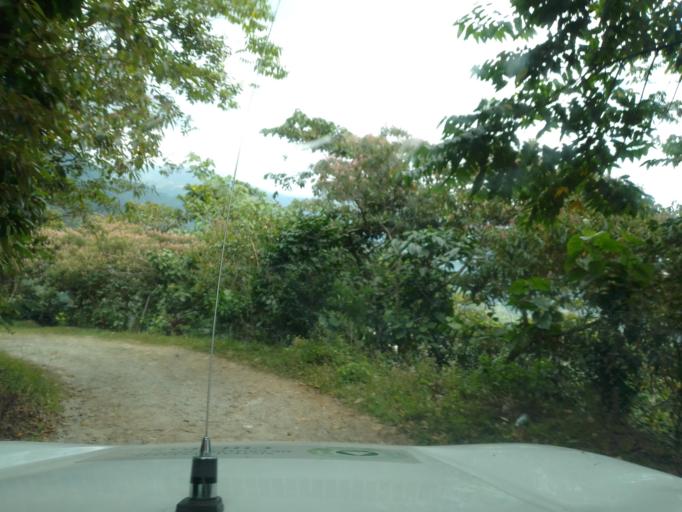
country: MX
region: Chiapas
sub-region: Union Juarez
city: Santo Domingo
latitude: 15.0568
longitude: -92.0973
